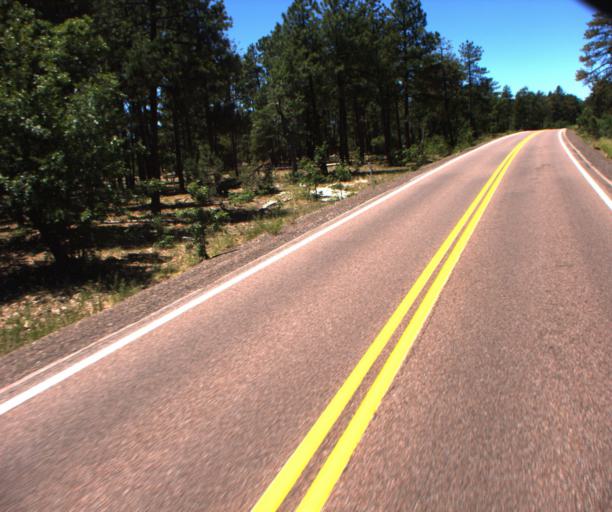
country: US
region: Arizona
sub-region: Gila County
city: Pine
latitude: 34.4404
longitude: -111.4803
